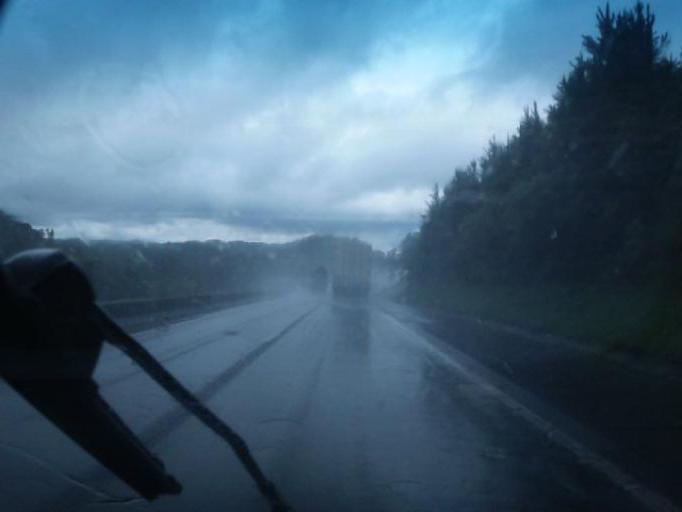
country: BR
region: Sao Paulo
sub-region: Cajati
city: Cajati
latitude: -24.9688
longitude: -48.3470
